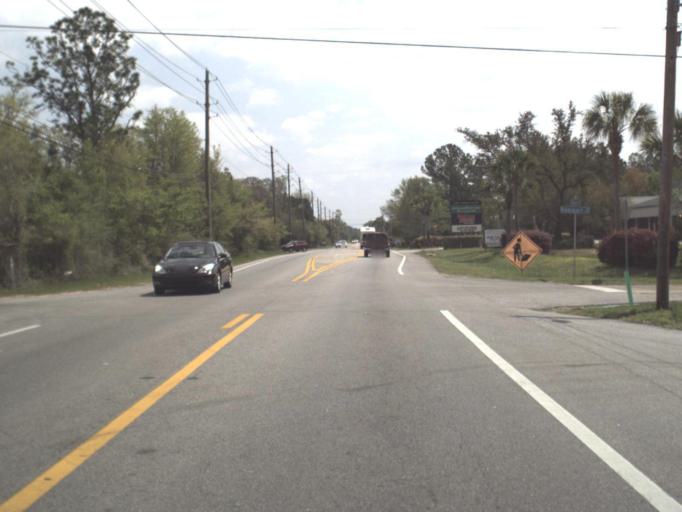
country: US
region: Florida
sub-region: Escambia County
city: Myrtle Grove
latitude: 30.3712
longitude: -87.3300
